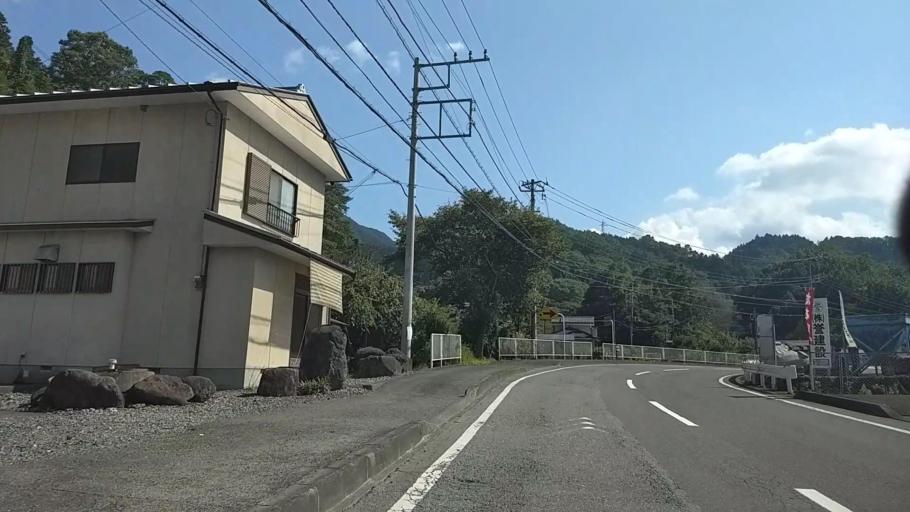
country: JP
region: Yamanashi
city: Fujikawaguchiko
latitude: 35.4080
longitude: 138.4564
